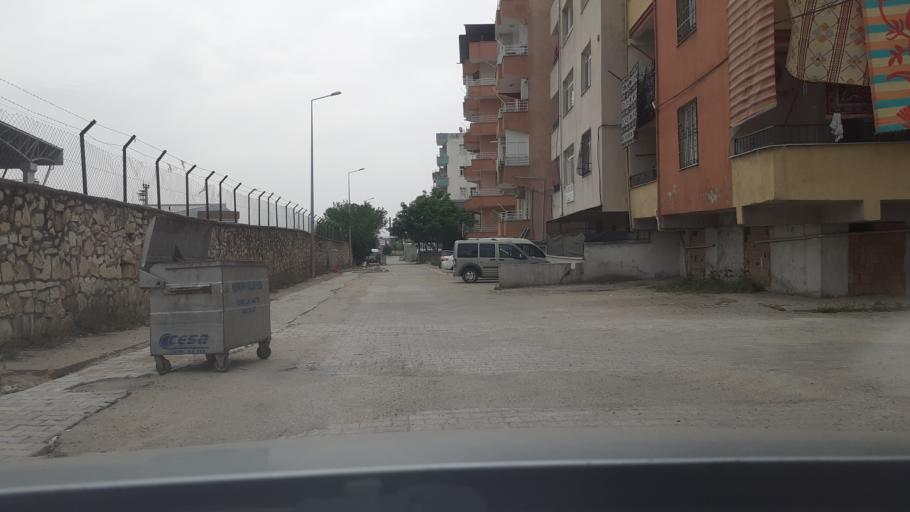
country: TR
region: Hatay
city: Kirikhan
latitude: 36.4922
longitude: 36.3678
